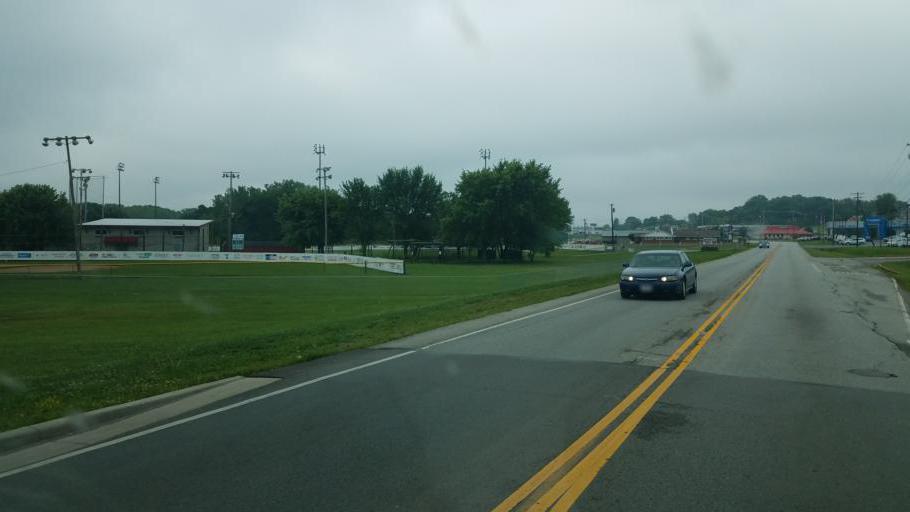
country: US
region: Ohio
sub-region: Highland County
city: Hillsboro
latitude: 39.2331
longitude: -83.6102
